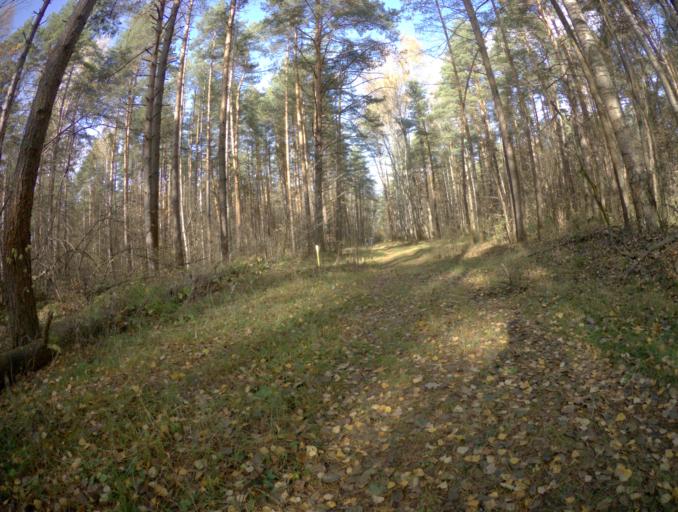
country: RU
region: Vladimir
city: Kommunar
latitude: 56.0785
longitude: 40.4417
